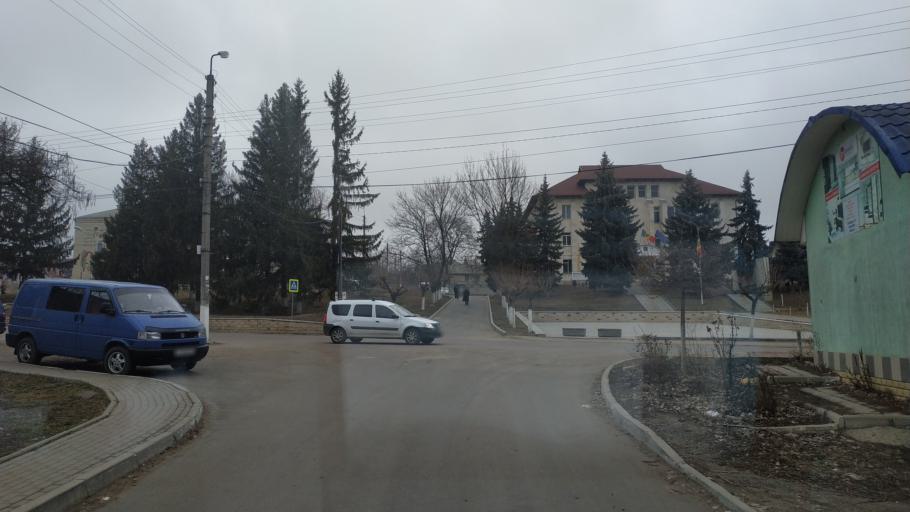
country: MD
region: Hincesti
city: Hincesti
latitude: 46.9036
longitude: 28.6734
